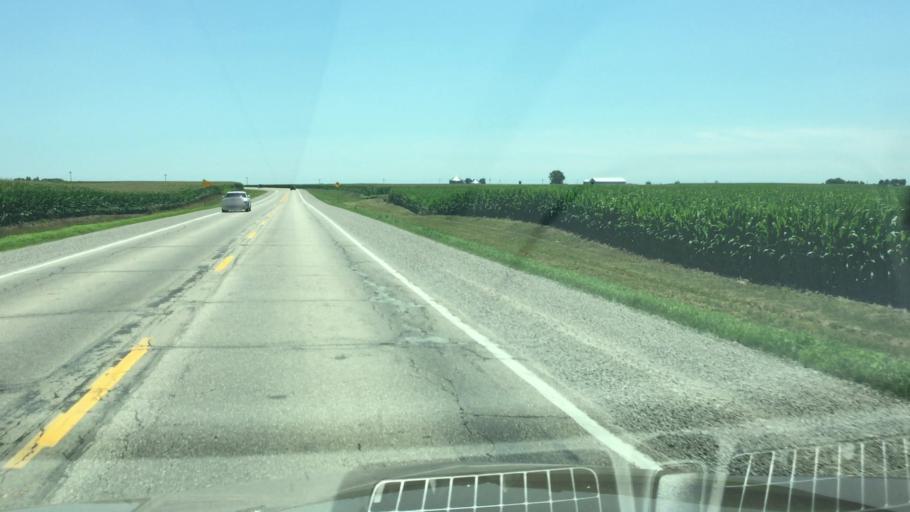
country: US
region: Iowa
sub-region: Cedar County
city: Mechanicsville
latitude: 41.8914
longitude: -91.2167
